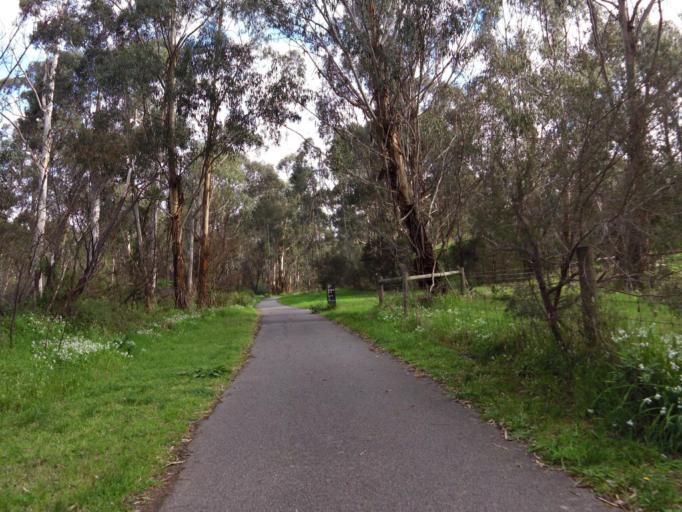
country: AU
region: Victoria
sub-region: Manningham
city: Donvale
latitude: -37.7587
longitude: 145.1824
